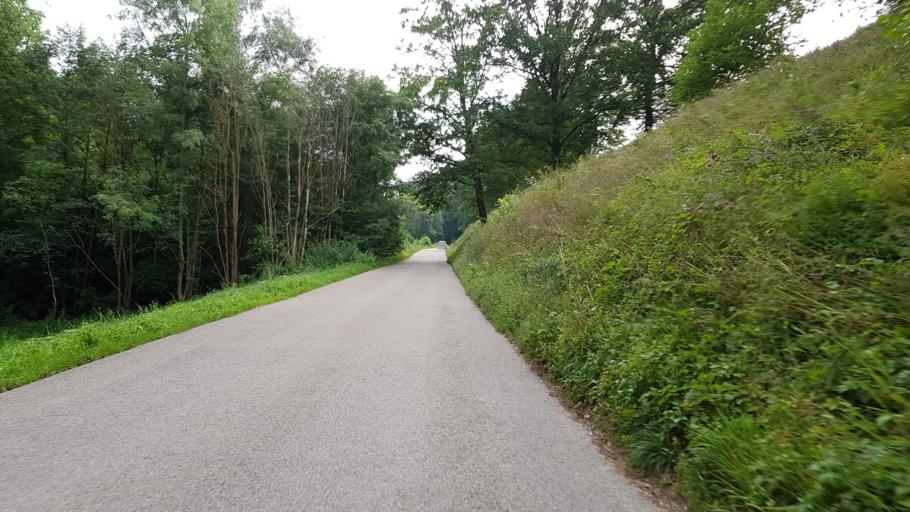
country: DE
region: Baden-Wuerttemberg
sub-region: Regierungsbezirk Stuttgart
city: Steinheim am der Murr
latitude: 48.9703
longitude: 9.3067
